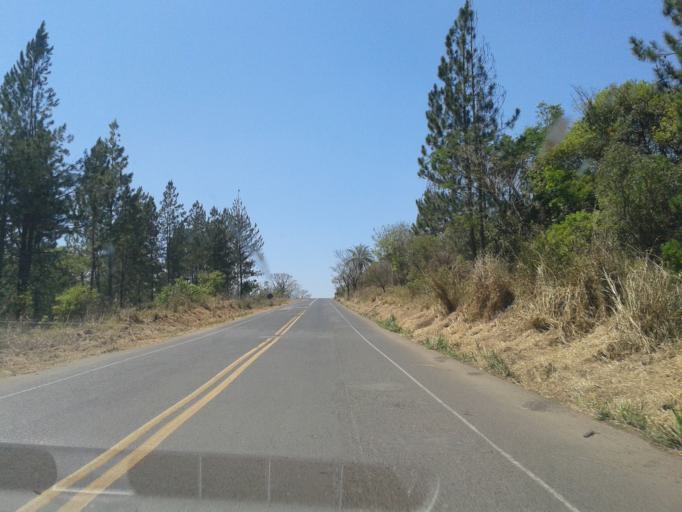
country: BR
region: Minas Gerais
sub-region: Araxa
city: Araxa
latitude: -19.4538
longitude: -47.1829
